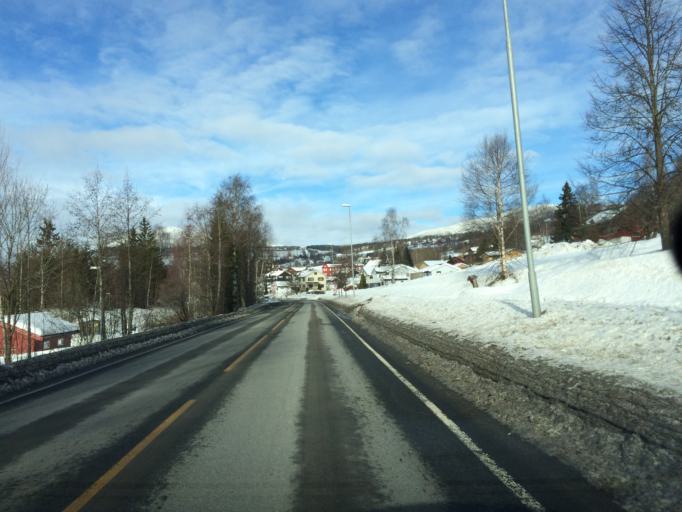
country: NO
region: Oppland
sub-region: Gausdal
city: Segalstad bru
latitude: 61.2122
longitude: 10.2936
